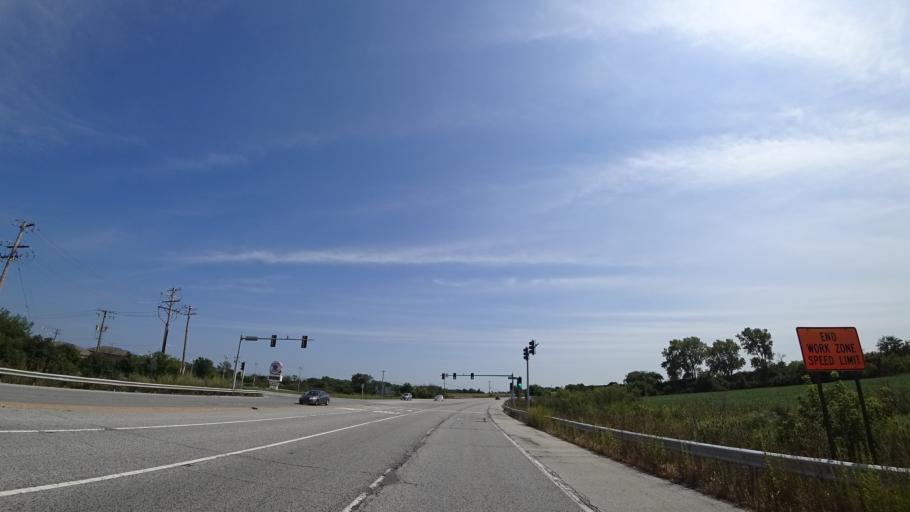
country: US
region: Illinois
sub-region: Will County
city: Frankfort Square
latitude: 41.5407
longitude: -87.7914
